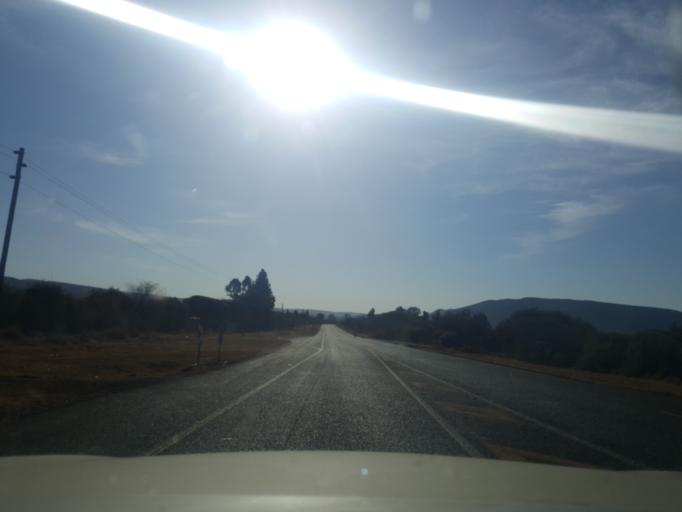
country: ZA
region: North-West
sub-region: Ngaka Modiri Molema District Municipality
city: Zeerust
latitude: -25.4605
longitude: 25.8815
